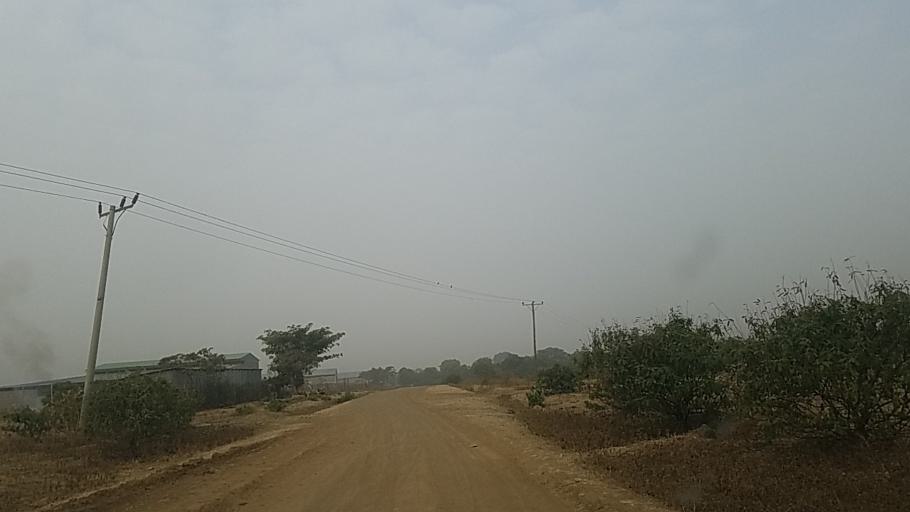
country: ET
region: Amhara
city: Bure
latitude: 10.9777
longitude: 36.4973
